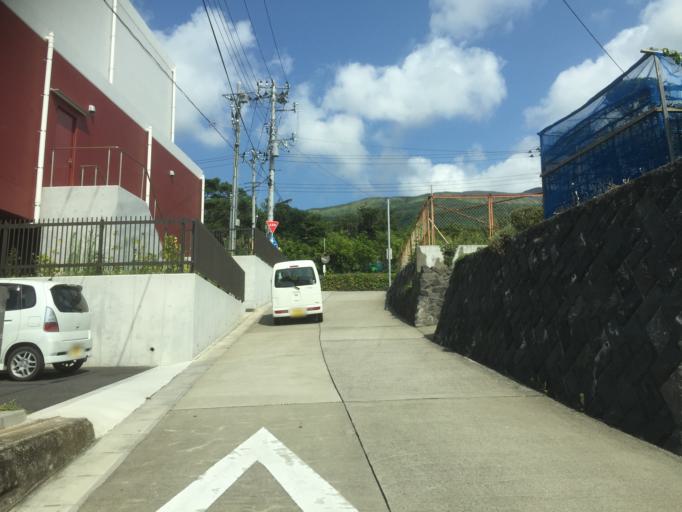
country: JP
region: Shizuoka
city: Shimoda
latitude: 34.0600
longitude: 139.5457
